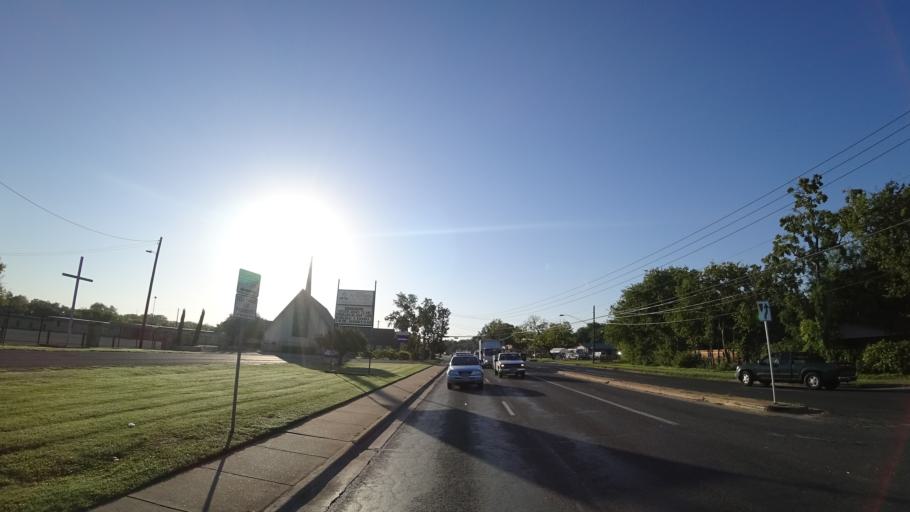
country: US
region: Texas
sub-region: Travis County
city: Wells Branch
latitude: 30.3615
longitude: -97.6942
